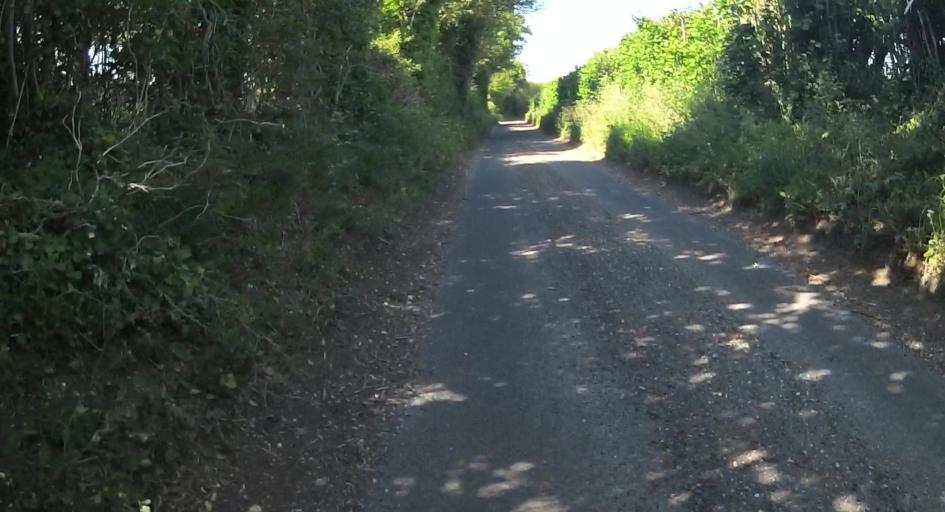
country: GB
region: England
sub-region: Hampshire
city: Overton
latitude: 51.2424
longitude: -1.3115
